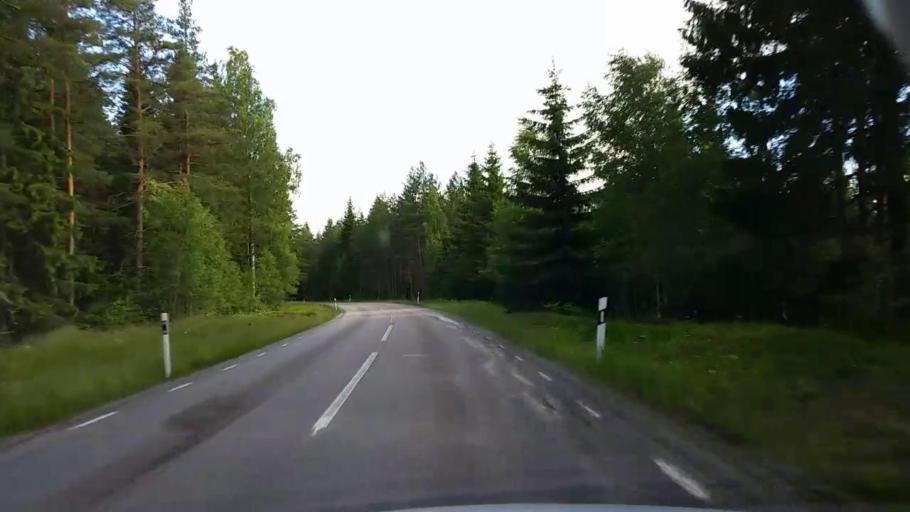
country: SE
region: Vaestmanland
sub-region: Fagersta Kommun
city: Fagersta
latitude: 59.9584
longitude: 15.7779
